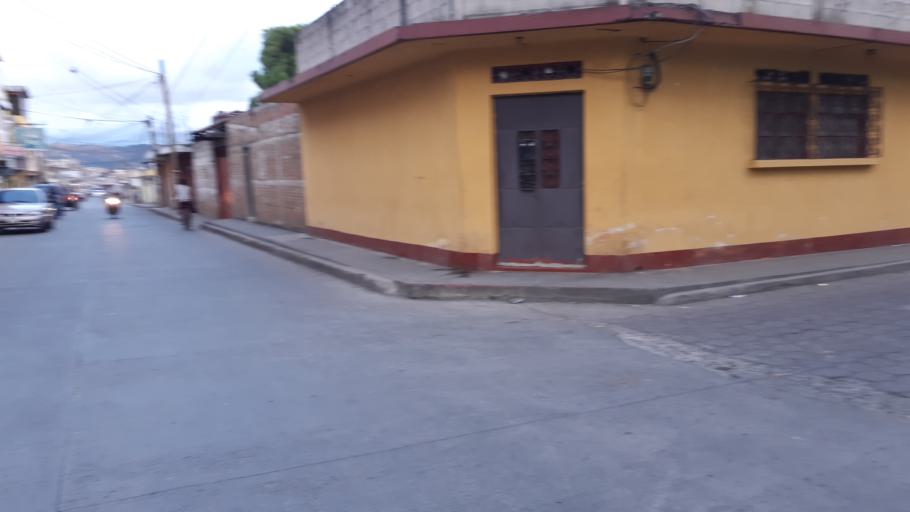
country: GT
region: Chimaltenango
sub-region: Municipio de Chimaltenango
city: Chimaltenango
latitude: 14.6639
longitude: -90.8202
